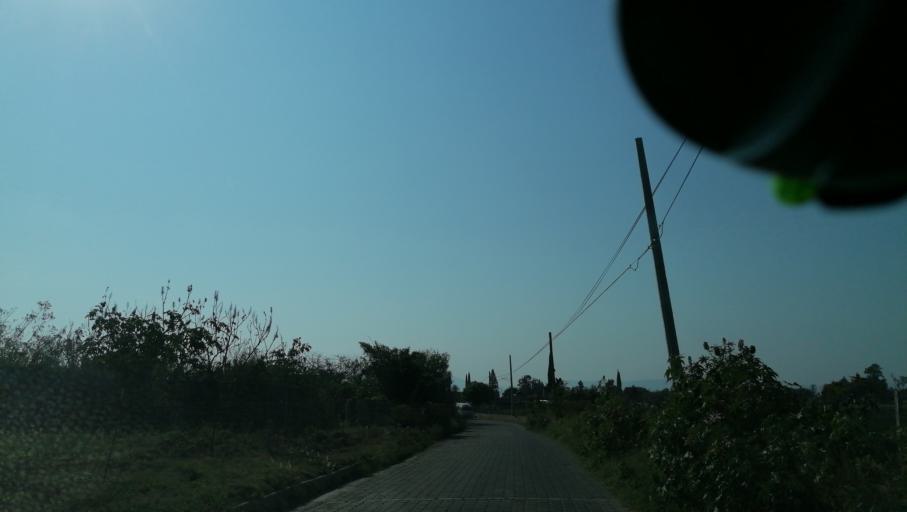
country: MX
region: Puebla
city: Atlixco
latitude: 18.9274
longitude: -98.4557
